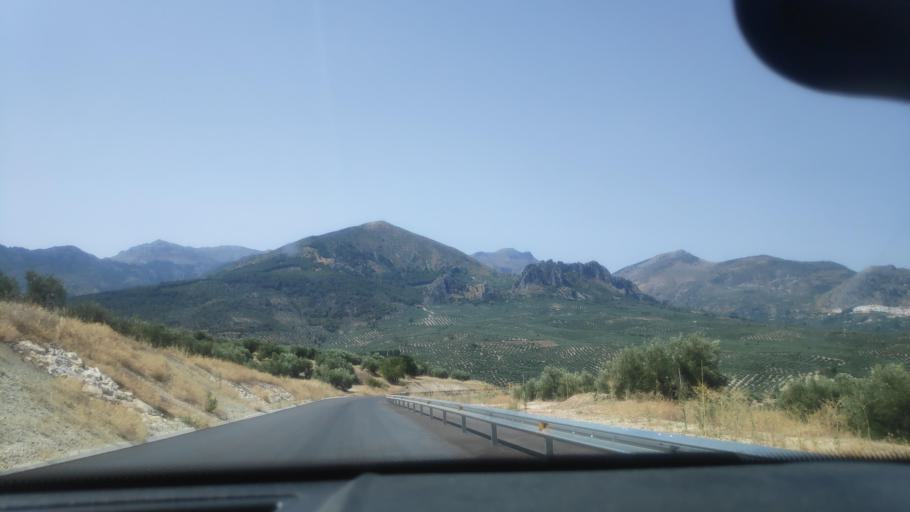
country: ES
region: Andalusia
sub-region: Provincia de Jaen
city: Jodar
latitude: 37.8116
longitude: -3.4126
